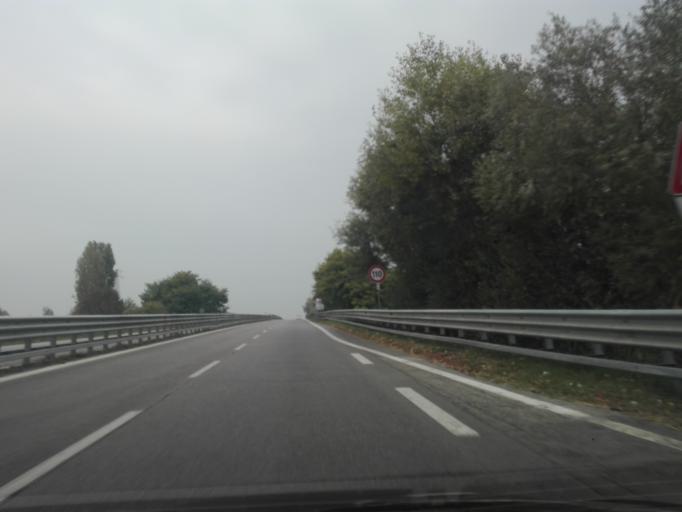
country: IT
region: Veneto
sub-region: Provincia di Verona
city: Legnago
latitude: 45.1647
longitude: 11.3023
